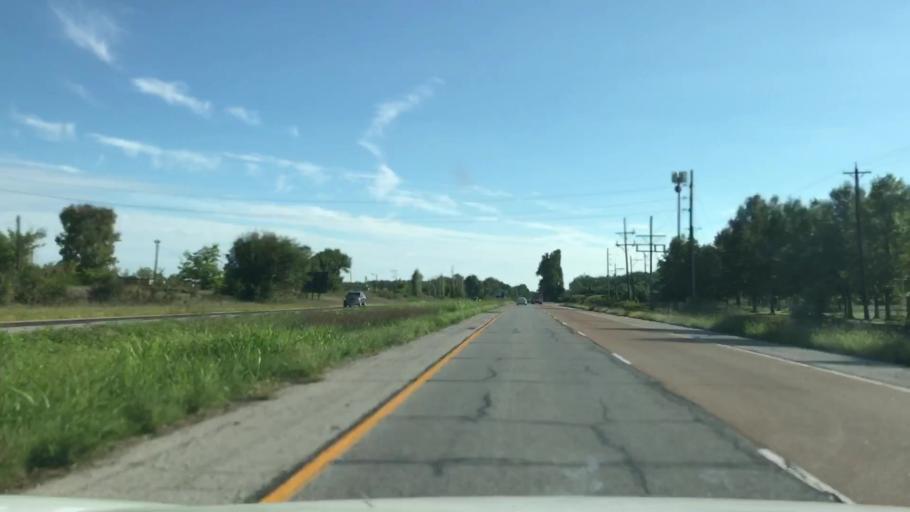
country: US
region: Illinois
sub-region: Madison County
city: Hartford
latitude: 38.8009
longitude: -90.1005
